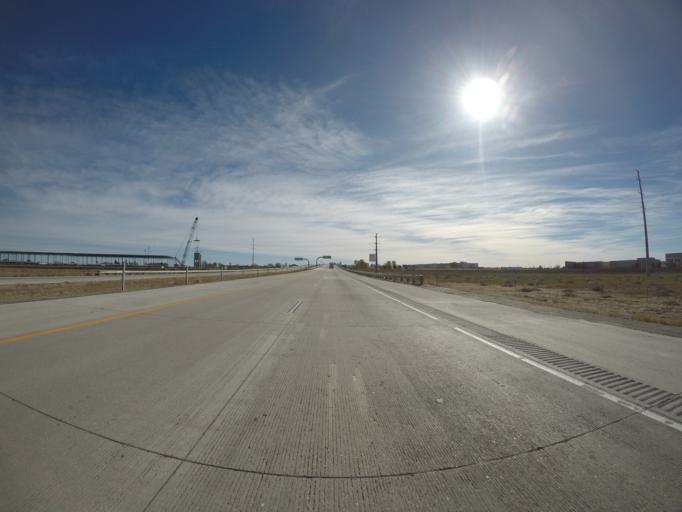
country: US
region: Colorado
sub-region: Adams County
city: Aurora
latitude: 39.7548
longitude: -104.7594
